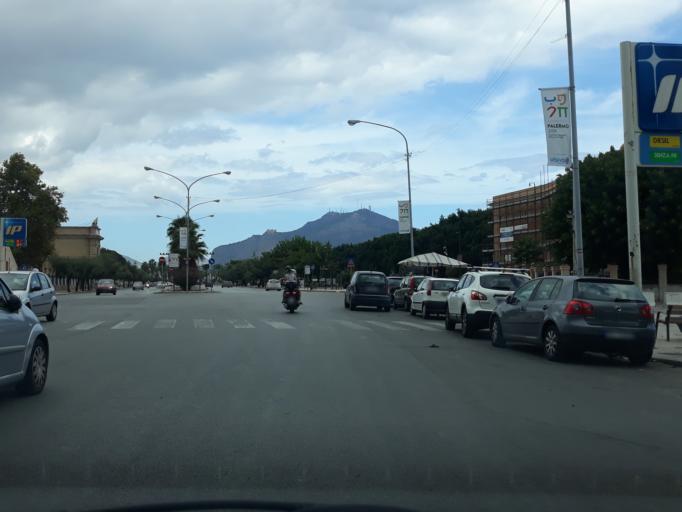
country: IT
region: Sicily
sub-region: Palermo
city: Palermo
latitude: 38.1126
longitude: 13.3782
